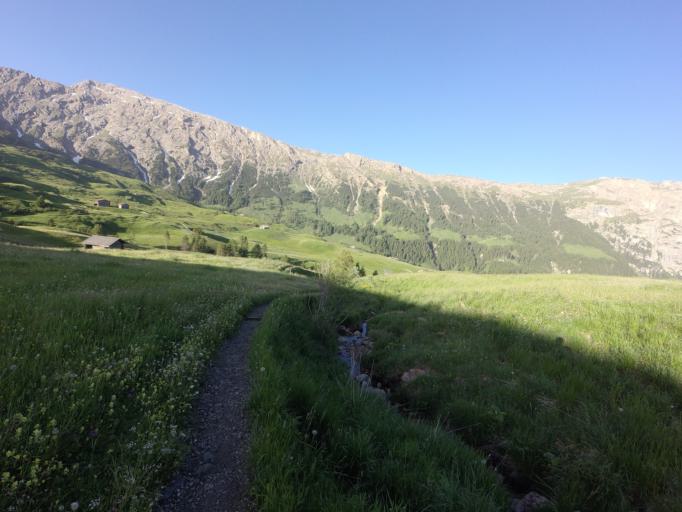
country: IT
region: Trentino-Alto Adige
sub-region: Bolzano
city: Siusi
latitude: 46.5205
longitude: 11.6135
